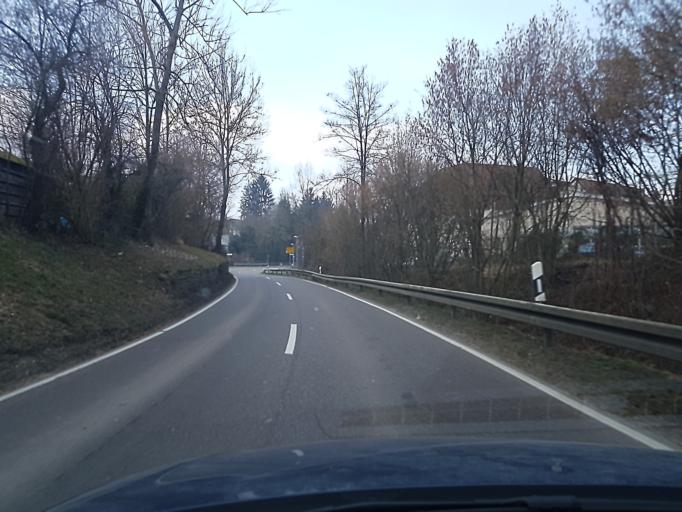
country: DE
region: Baden-Wuerttemberg
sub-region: Regierungsbezirk Stuttgart
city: Eberdingen
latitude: 48.9112
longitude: 8.9801
